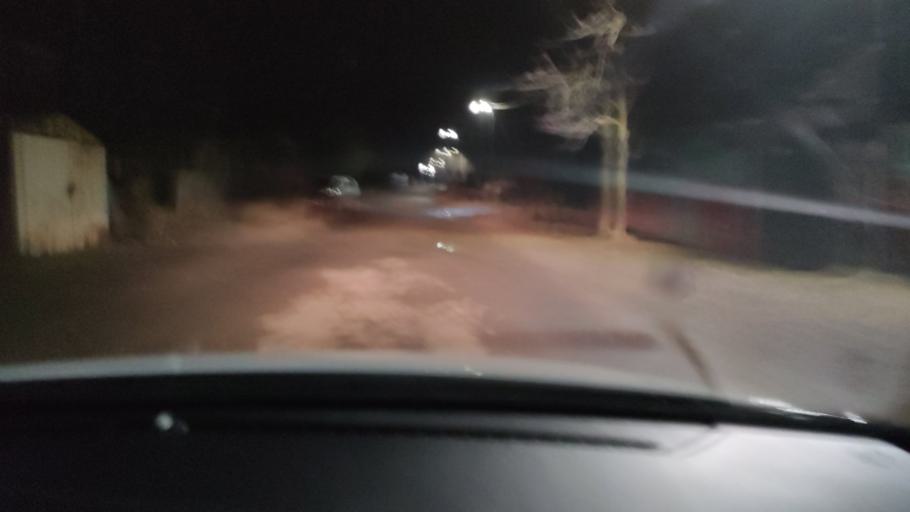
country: RU
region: Tatarstan
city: Vysokaya Gora
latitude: 55.8456
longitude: 49.2174
